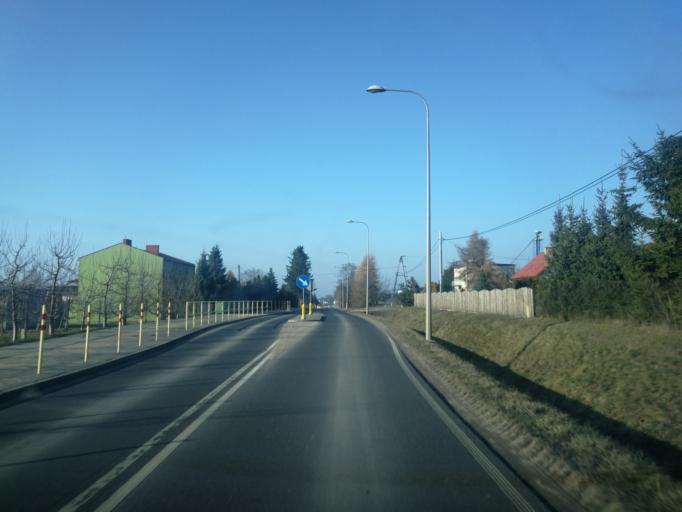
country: PL
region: Warmian-Masurian Voivodeship
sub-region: Powiat ilawski
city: Lubawa
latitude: 53.4813
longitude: 19.7632
